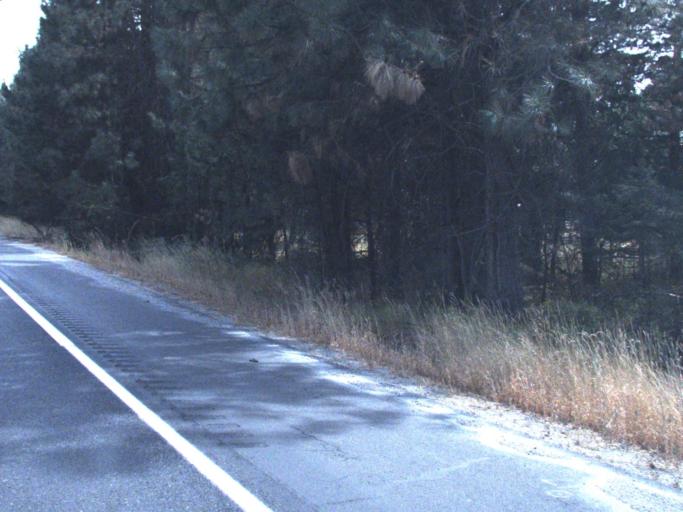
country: US
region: Washington
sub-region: Spokane County
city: Deer Park
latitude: 47.9620
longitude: -117.4990
